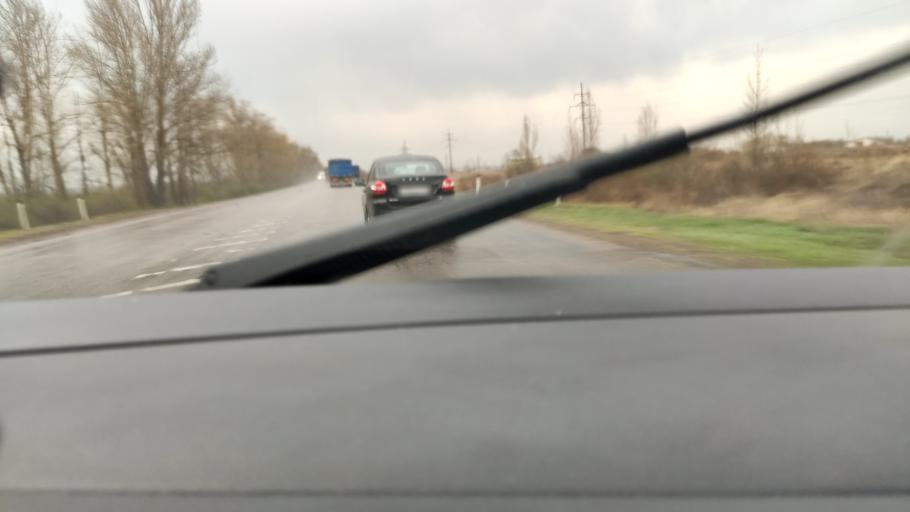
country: RU
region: Voronezj
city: Maslovka
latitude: 51.5125
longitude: 39.3031
